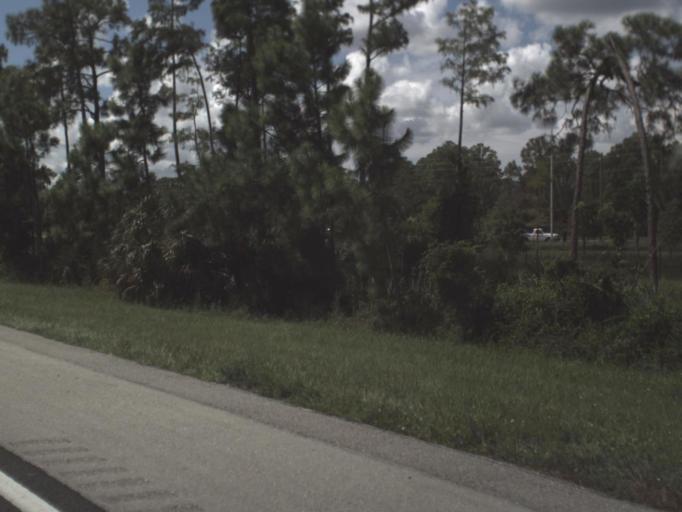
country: US
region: Florida
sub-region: Lee County
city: Three Oaks
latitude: 26.4665
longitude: -81.7894
